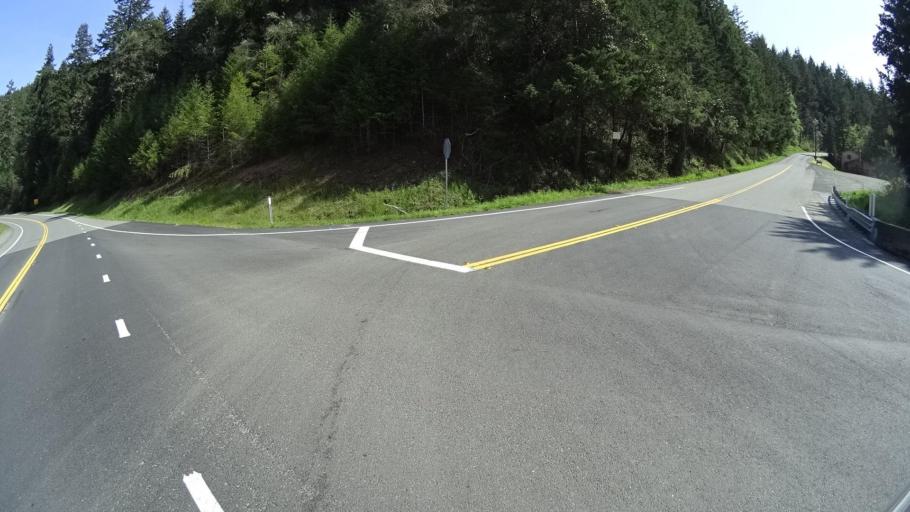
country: US
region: California
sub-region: Humboldt County
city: Hydesville
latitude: 40.4685
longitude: -123.7994
